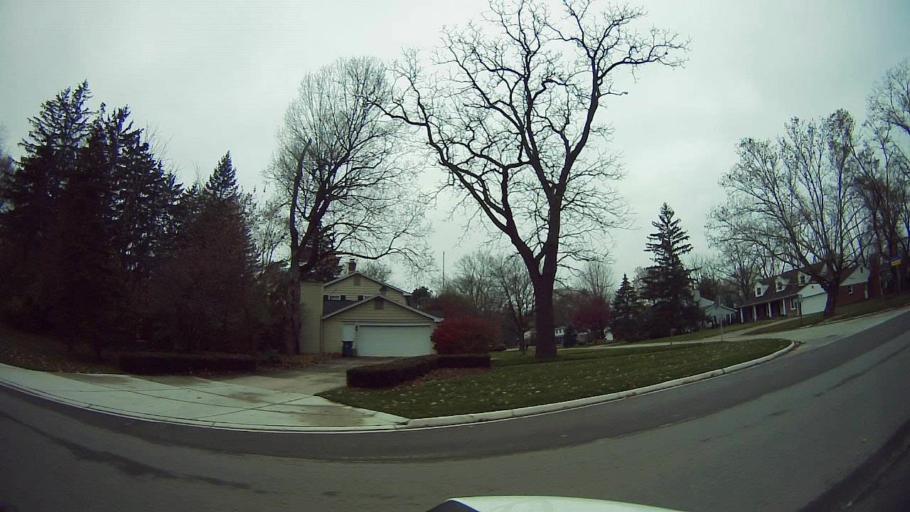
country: US
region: Michigan
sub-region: Oakland County
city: Bingham Farms
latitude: 42.5205
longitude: -83.2630
